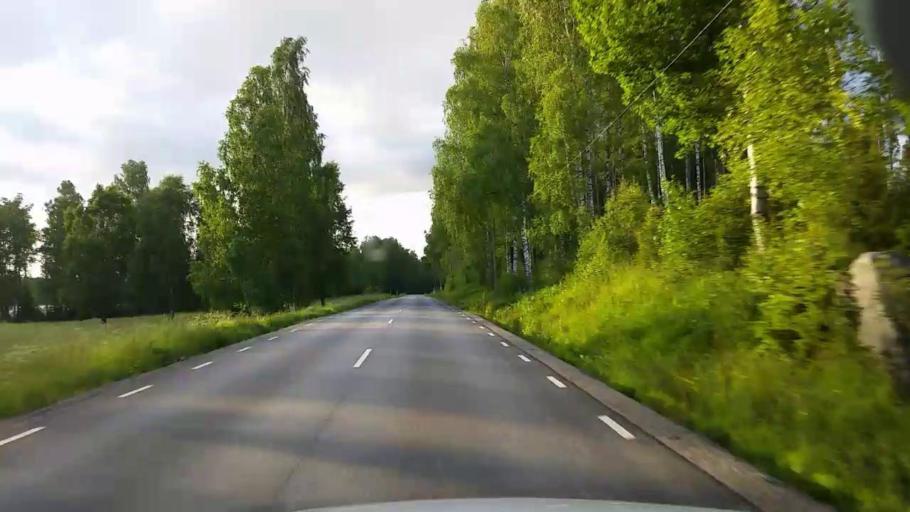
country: SE
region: Vaestmanland
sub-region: Kopings Kommun
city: Kolsva
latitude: 59.7348
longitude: 15.8256
